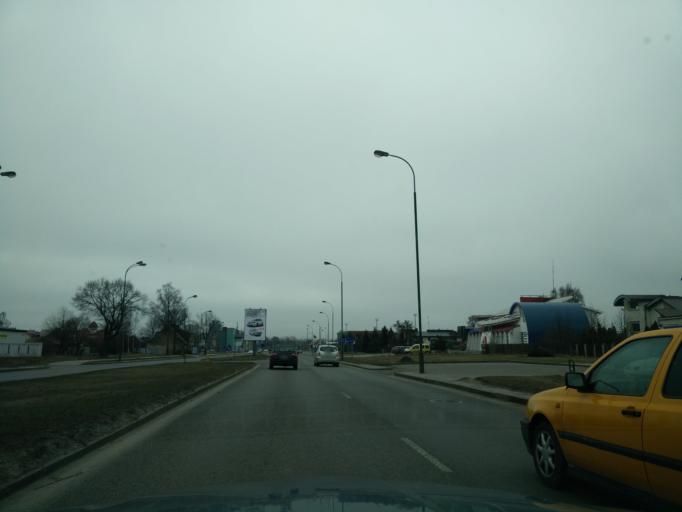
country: LT
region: Klaipedos apskritis
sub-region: Klaipeda
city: Klaipeda
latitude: 55.6912
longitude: 21.1433
